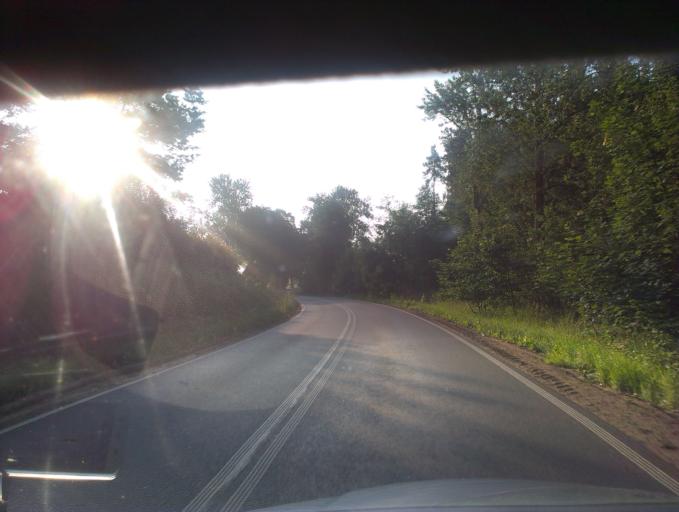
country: PL
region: West Pomeranian Voivodeship
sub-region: Powiat szczecinecki
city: Barwice
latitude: 53.7231
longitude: 16.3980
